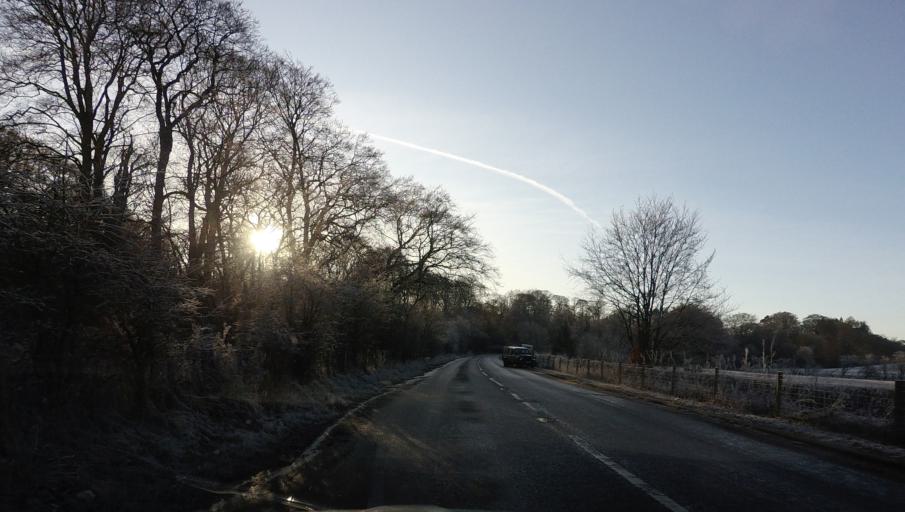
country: GB
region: Scotland
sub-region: North Lanarkshire
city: Newmains
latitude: 55.7978
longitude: -3.8503
